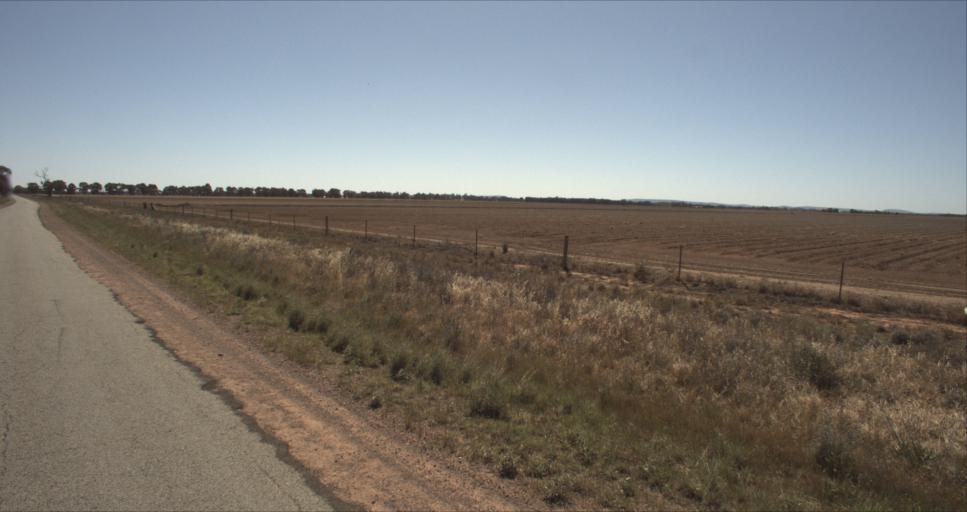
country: AU
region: New South Wales
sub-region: Leeton
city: Leeton
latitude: -34.5587
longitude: 146.3131
